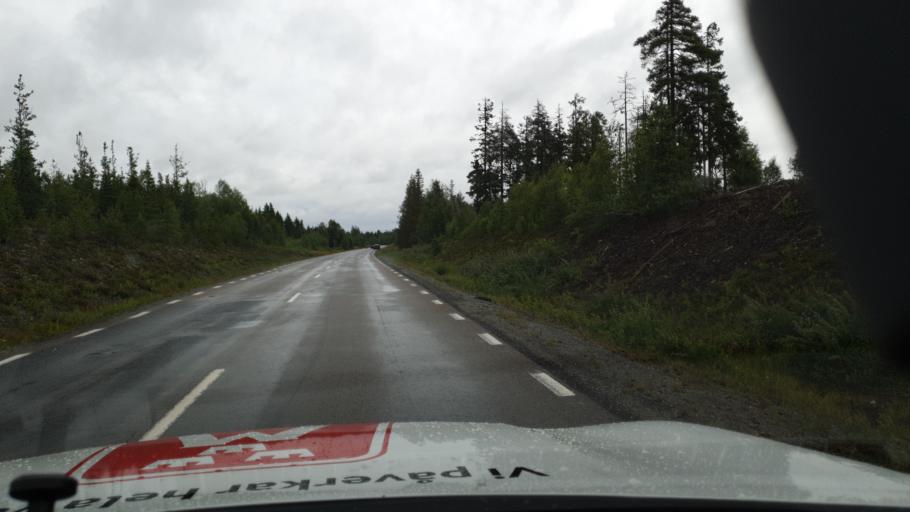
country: SE
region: Vaesterbotten
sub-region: Umea Kommun
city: Saevar
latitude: 63.9129
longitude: 20.5331
